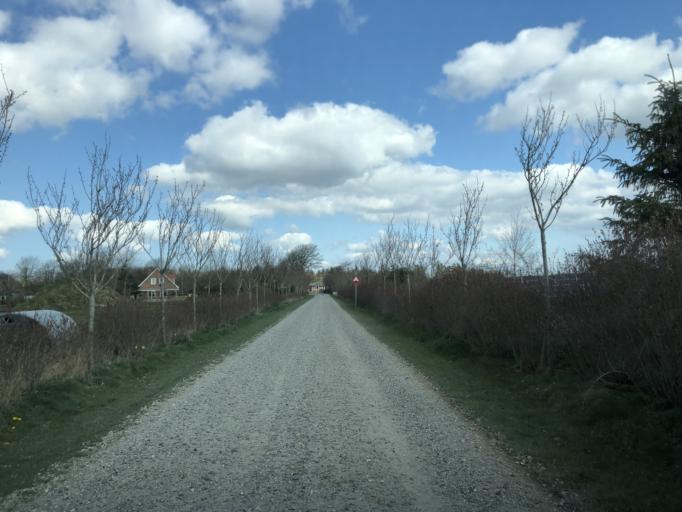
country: DK
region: Central Jutland
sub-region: Holstebro Kommune
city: Ulfborg
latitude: 56.3928
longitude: 8.2144
